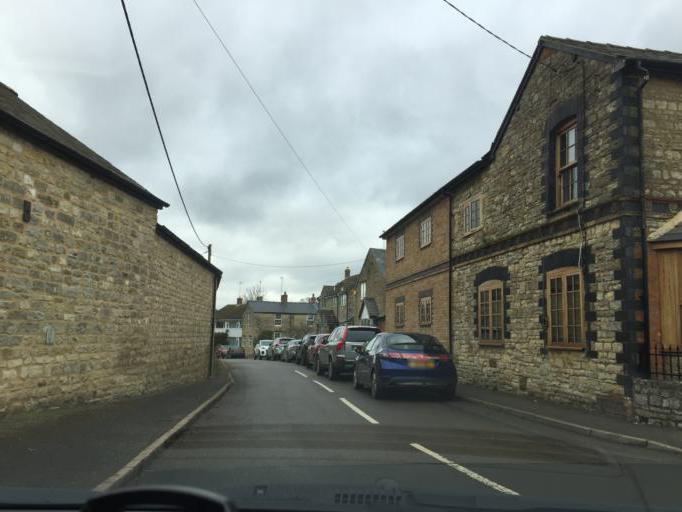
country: GB
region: England
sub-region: Northamptonshire
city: Silverstone
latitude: 52.0687
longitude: -1.0820
